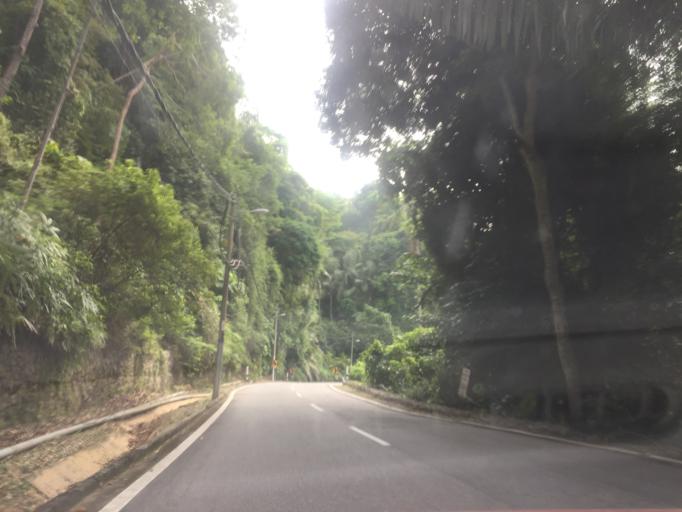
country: MY
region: Perak
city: Lumut
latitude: 4.2402
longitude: 100.5482
